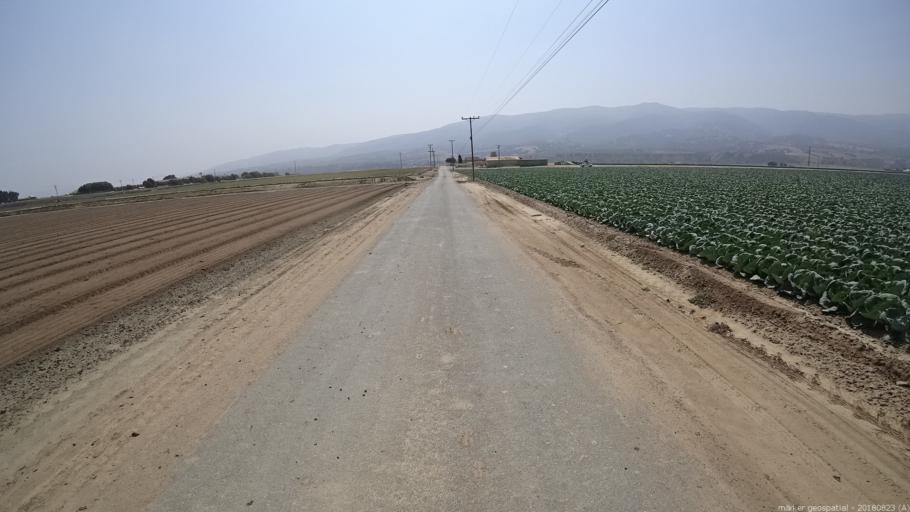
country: US
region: California
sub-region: Monterey County
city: Soledad
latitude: 36.4100
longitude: -121.3561
